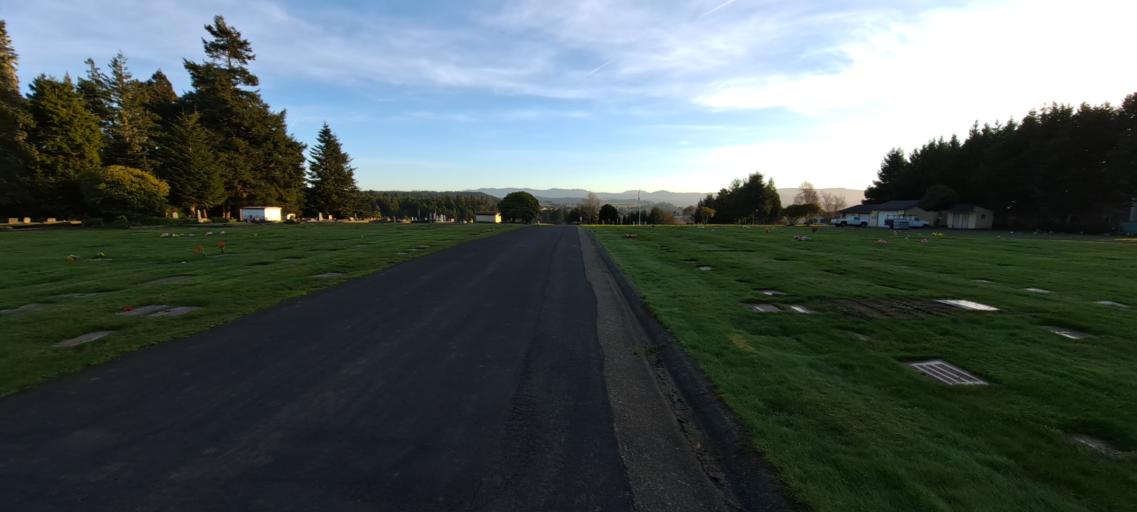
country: US
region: California
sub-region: Humboldt County
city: Fortuna
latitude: 40.5984
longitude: -124.1319
